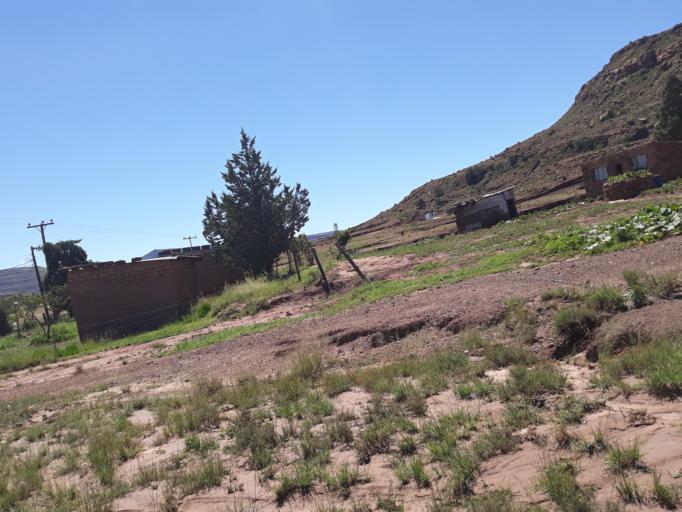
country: LS
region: Quthing
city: Quthing
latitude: -30.3395
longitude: 27.5397
